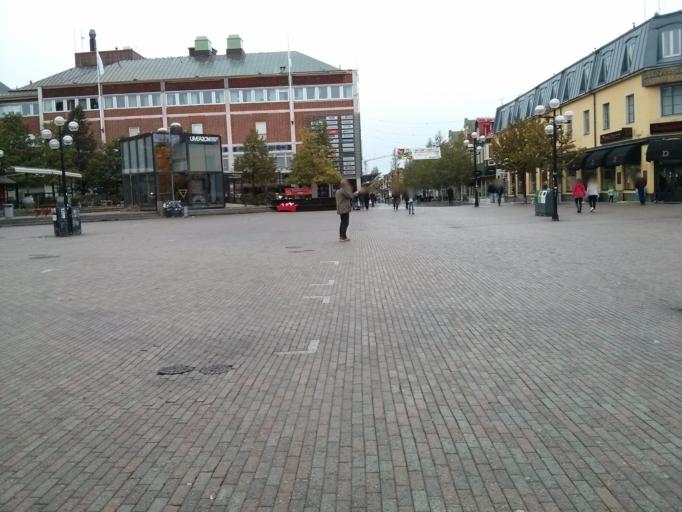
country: SE
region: Vaesterbotten
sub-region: Umea Kommun
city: Umea
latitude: 63.8258
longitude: 20.2637
